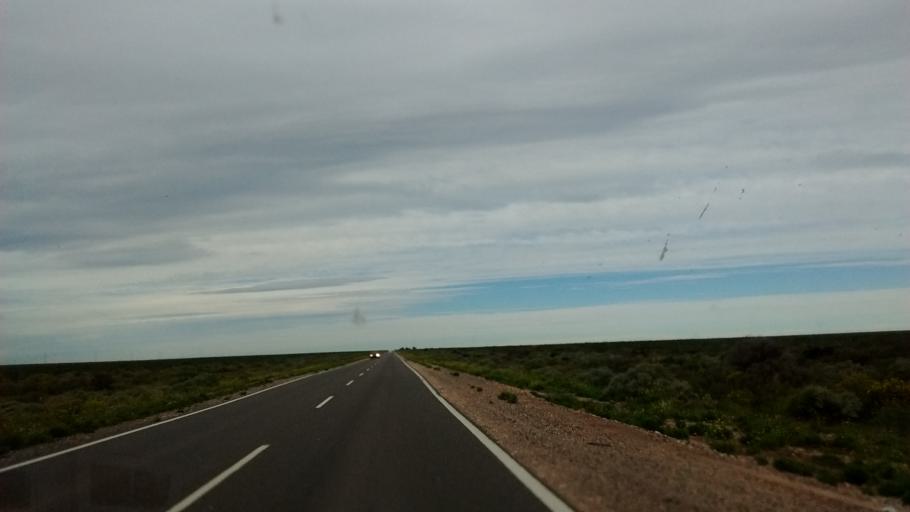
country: AR
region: Rio Negro
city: Contraalmirante Cordero
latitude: -38.3674
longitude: -68.0196
